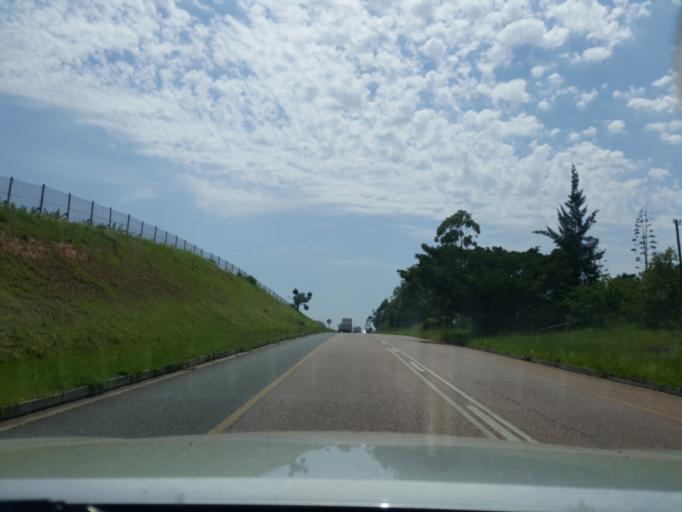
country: ZA
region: Mpumalanga
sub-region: Ehlanzeni District
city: White River
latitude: -25.1151
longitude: 31.0479
